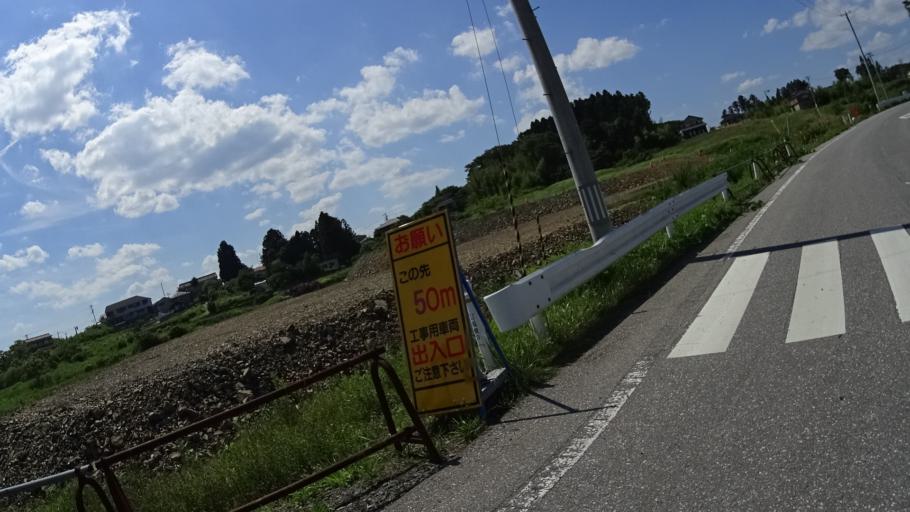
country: JP
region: Iwate
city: Ofunato
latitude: 38.8503
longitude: 141.6221
